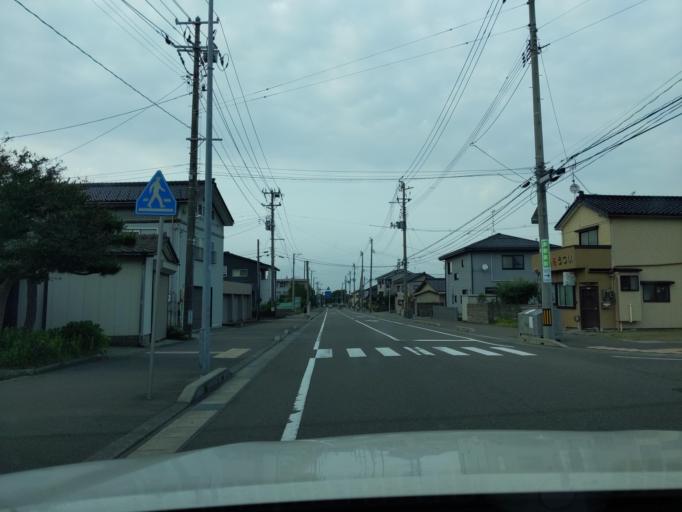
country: JP
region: Niigata
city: Kashiwazaki
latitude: 37.3805
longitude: 138.5650
